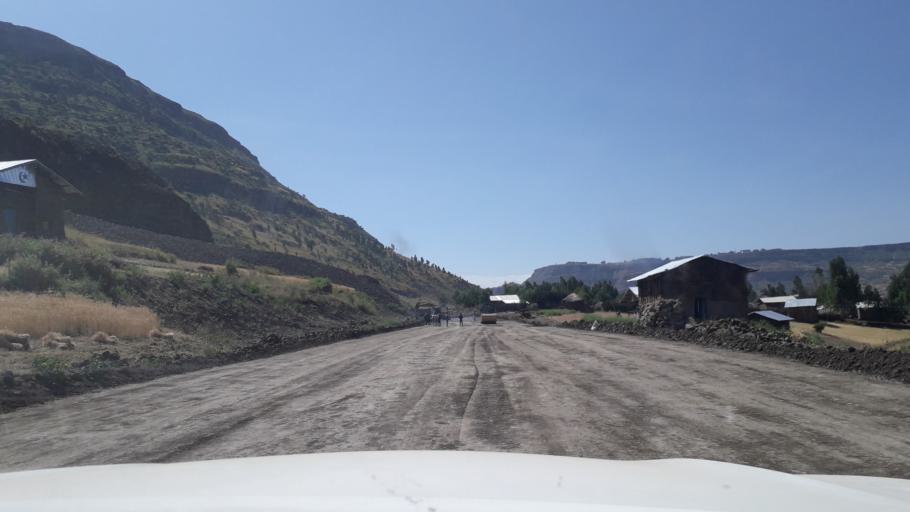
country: ET
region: Amhara
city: Lalibela
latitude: 11.5178
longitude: 39.0008
